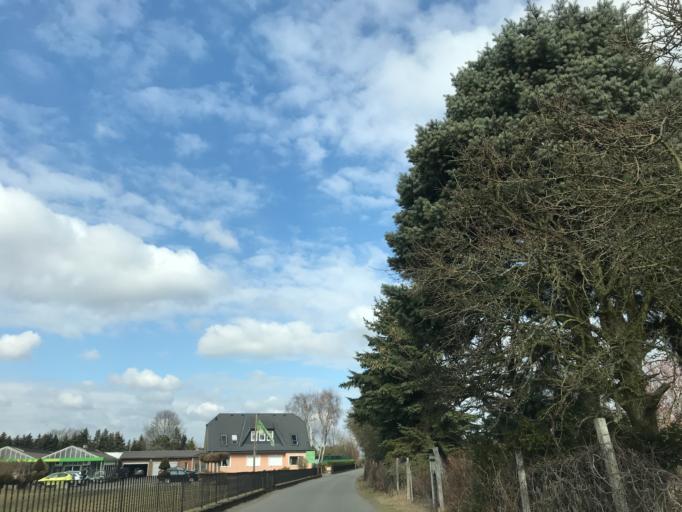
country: DE
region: Berlin
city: Kladow
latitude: 52.4617
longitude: 13.1419
